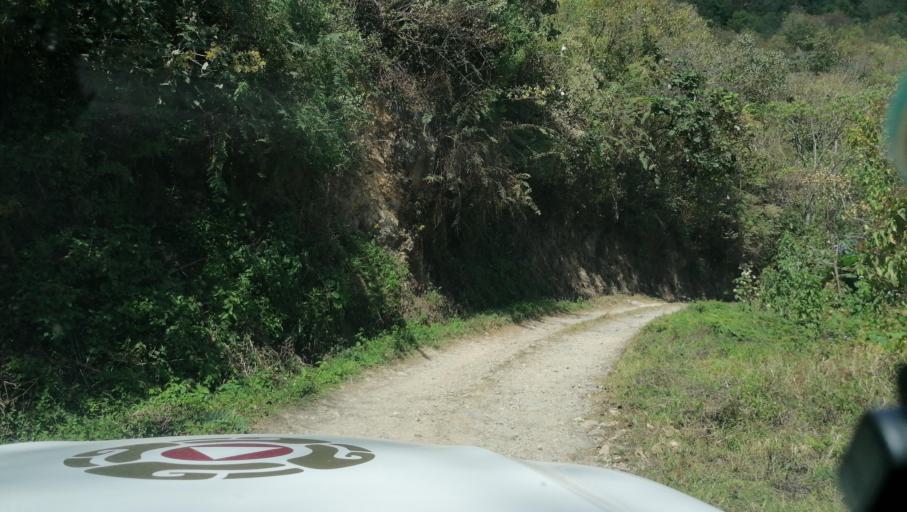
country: GT
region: San Marcos
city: Tacana
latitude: 15.2066
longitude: -92.2160
